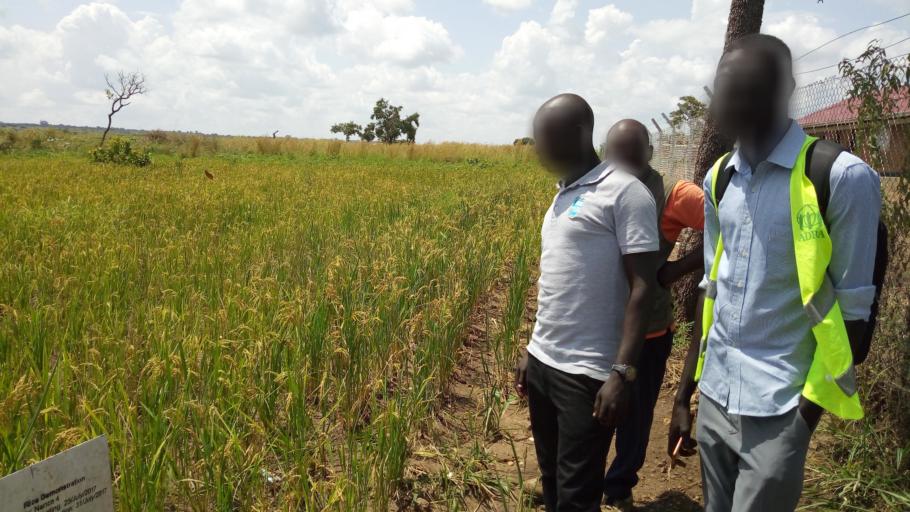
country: UG
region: Northern Region
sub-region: Yumbe District
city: Yumbe
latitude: 3.5249
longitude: 31.3467
